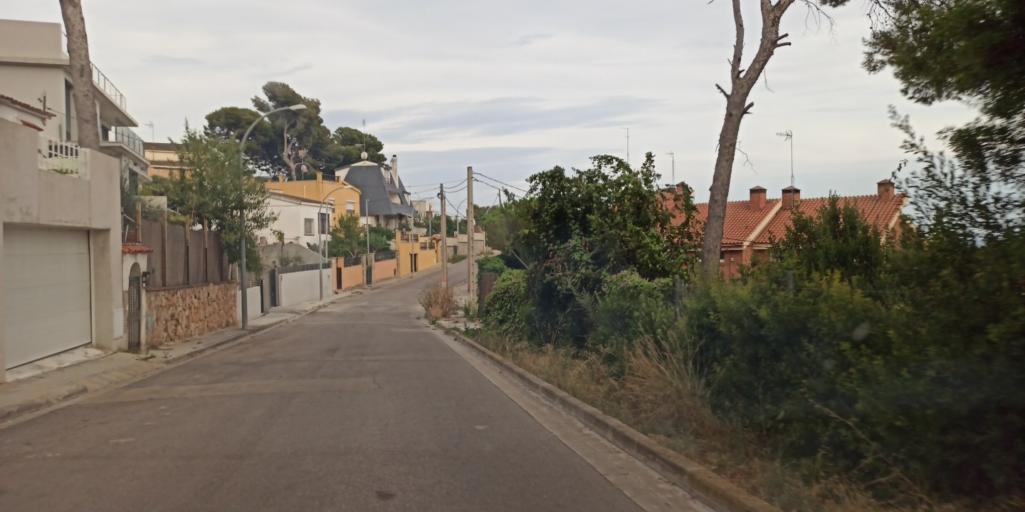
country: ES
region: Catalonia
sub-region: Provincia de Barcelona
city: Castelldefels
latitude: 41.2840
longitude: 1.9671
